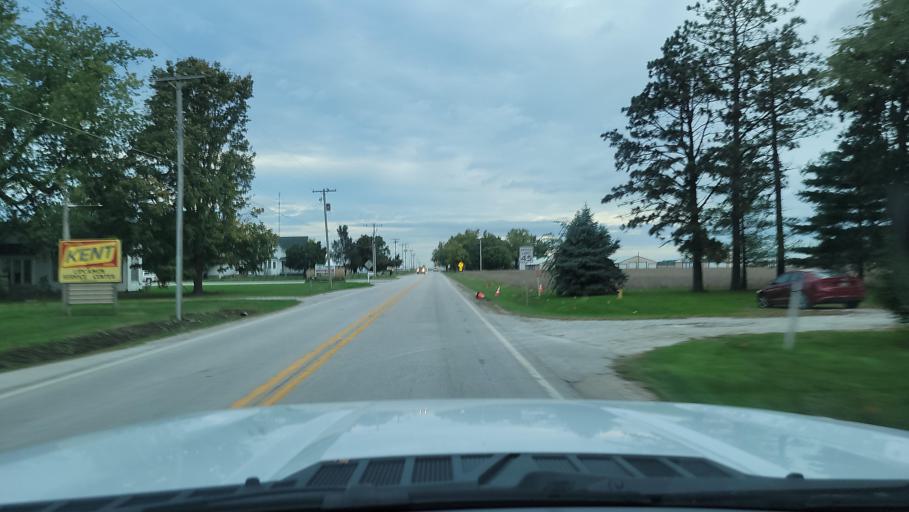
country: US
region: Illinois
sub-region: Schuyler County
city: Rushville
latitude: 40.1314
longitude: -90.5623
